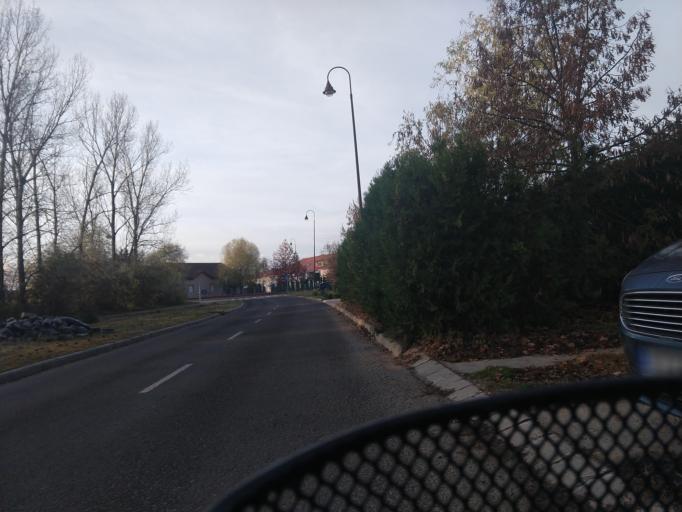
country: HU
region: Pest
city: Veresegyhaz
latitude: 47.6596
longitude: 19.2688
